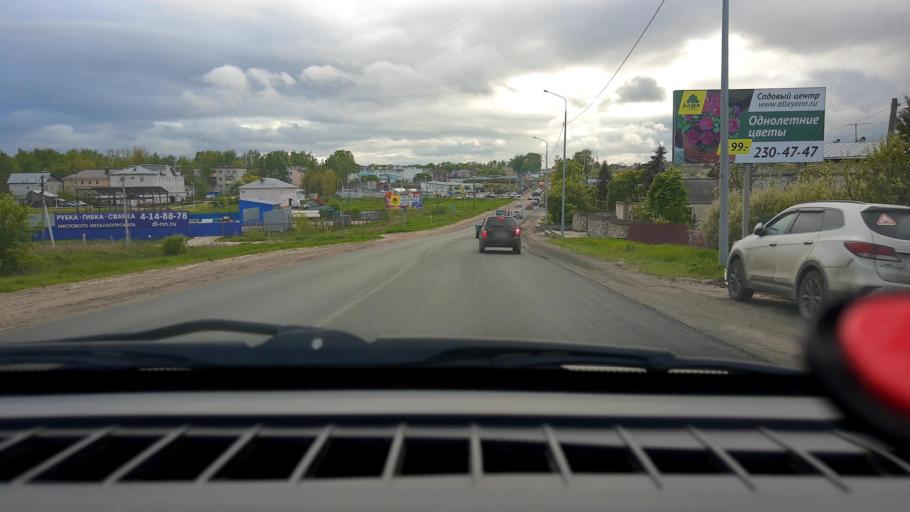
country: RU
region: Nizjnij Novgorod
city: Burevestnik
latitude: 56.2079
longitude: 43.8832
